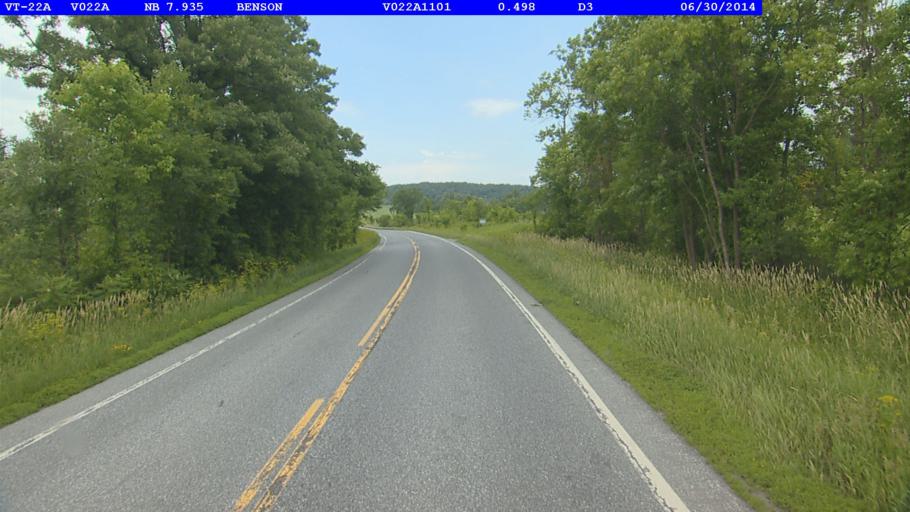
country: US
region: Vermont
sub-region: Rutland County
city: Fair Haven
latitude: 43.6765
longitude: -73.2884
